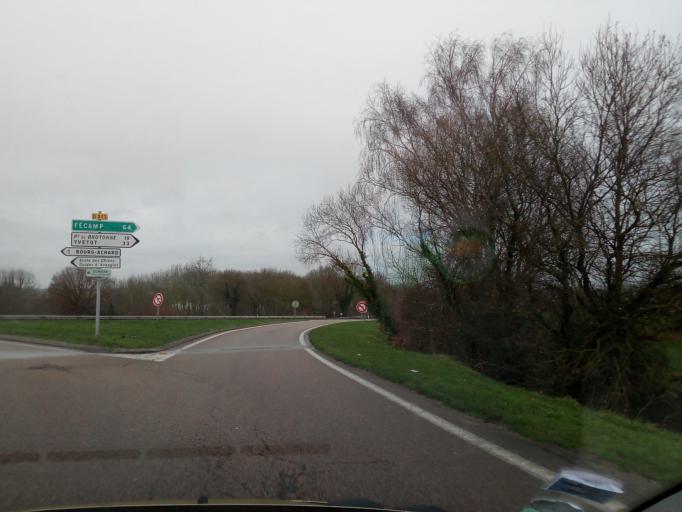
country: FR
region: Haute-Normandie
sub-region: Departement de l'Eure
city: Bourg-Achard
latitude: 49.3674
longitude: 0.8149
